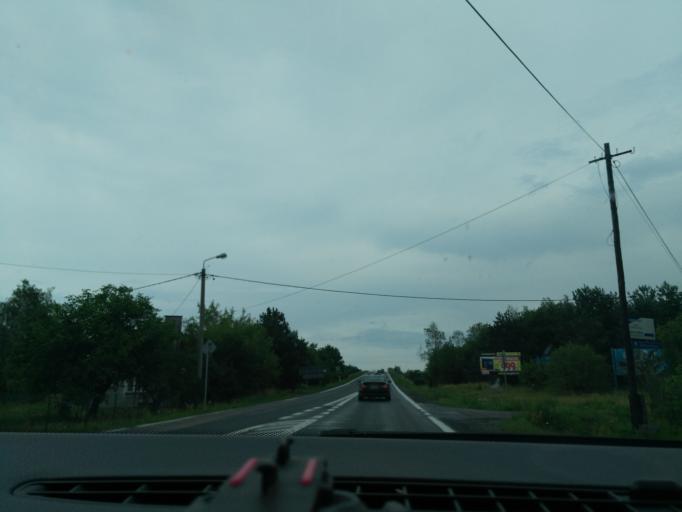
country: PL
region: Subcarpathian Voivodeship
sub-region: Powiat nizanski
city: Nisko
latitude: 50.5086
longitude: 22.1443
